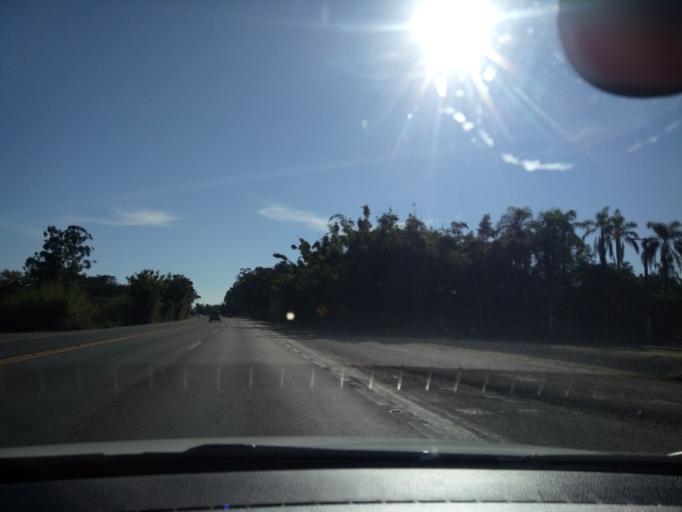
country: BR
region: Rio Grande do Sul
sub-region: Esteio
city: Esteio
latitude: -29.8311
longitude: -51.3180
